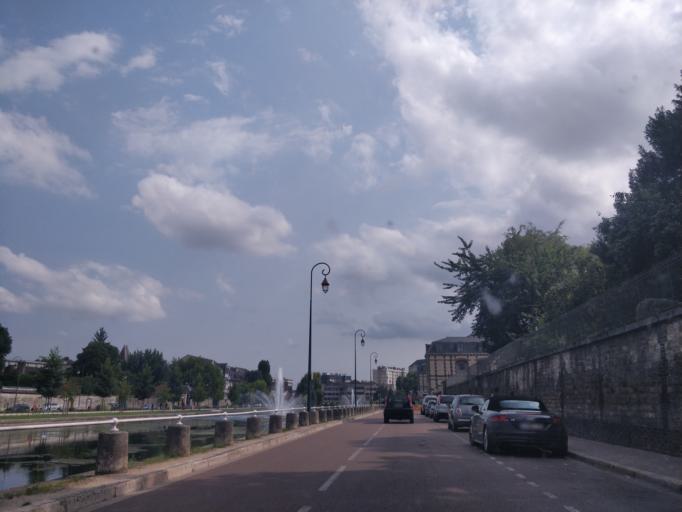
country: FR
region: Champagne-Ardenne
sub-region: Departement de l'Aube
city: Troyes
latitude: 48.2977
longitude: 4.0793
